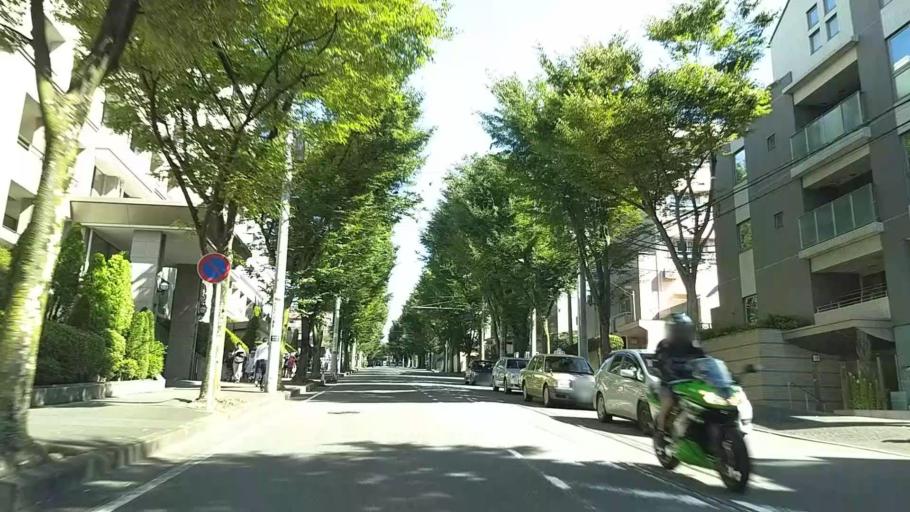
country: JP
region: Tokyo
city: Chofugaoka
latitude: 35.5722
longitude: 139.5549
